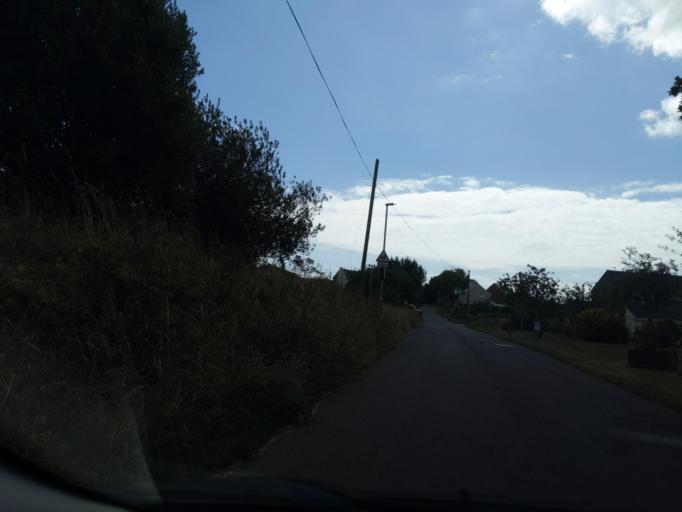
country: GB
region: England
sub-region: Devon
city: Modbury
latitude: 50.3523
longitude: -3.8887
